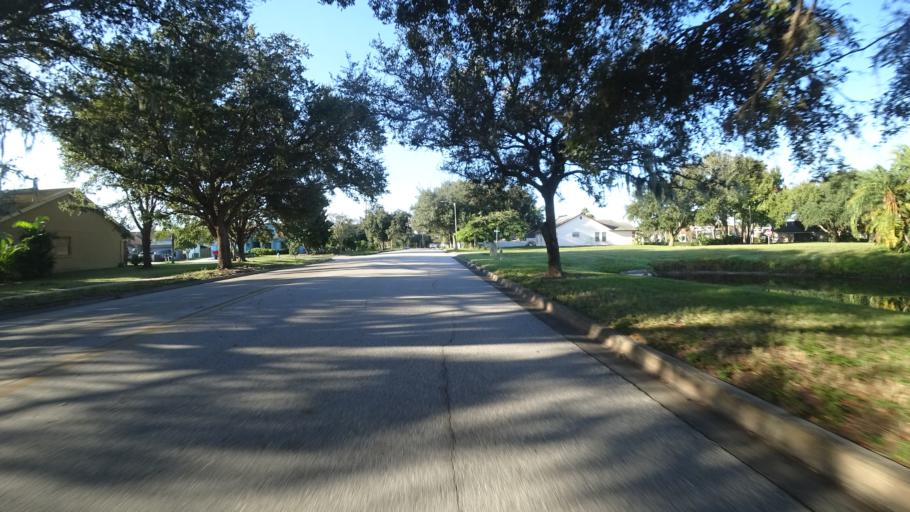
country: US
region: Florida
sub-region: Manatee County
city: Ellenton
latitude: 27.4920
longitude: -82.5009
